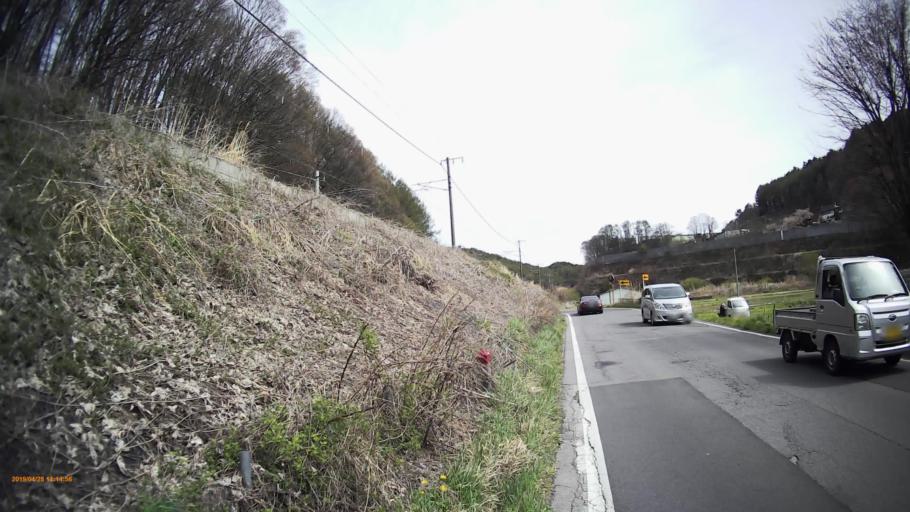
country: JP
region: Nagano
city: Chino
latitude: 35.9775
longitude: 138.1693
